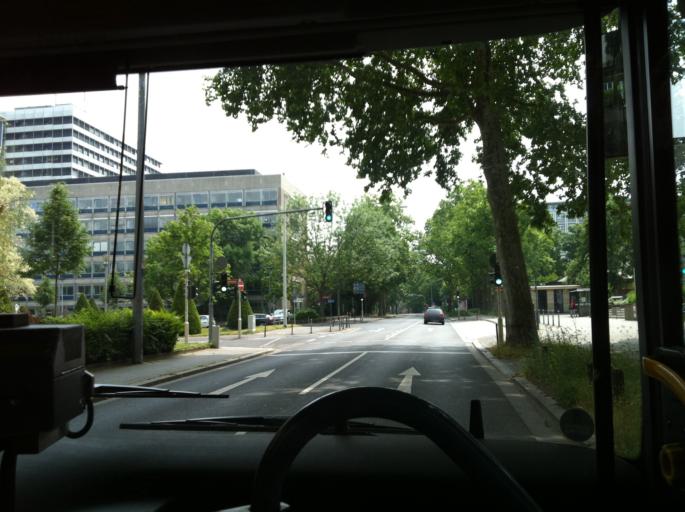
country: DE
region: Rheinland-Pfalz
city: Mainz
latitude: 49.9951
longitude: 8.2573
